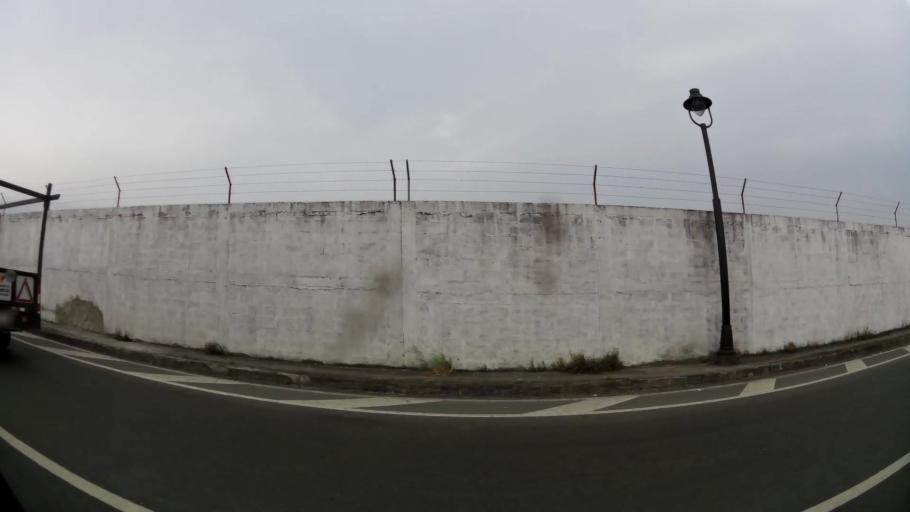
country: EC
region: Guayas
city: Eloy Alfaro
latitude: -2.1464
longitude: -79.8799
